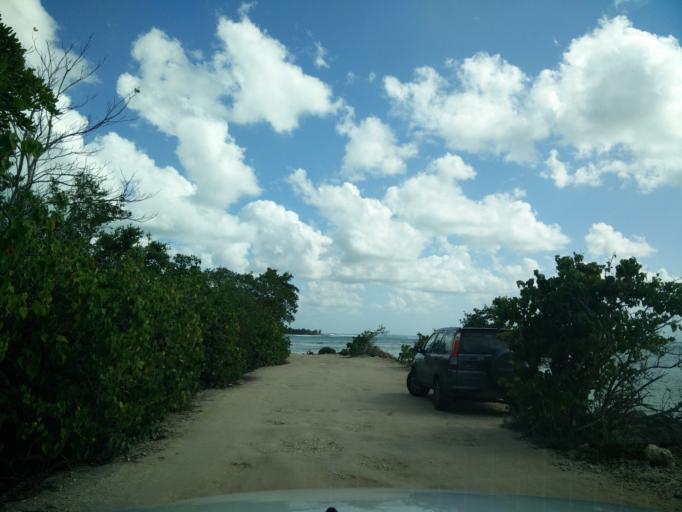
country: GP
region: Guadeloupe
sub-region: Guadeloupe
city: Port-Louis
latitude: 16.4304
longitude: -61.5366
